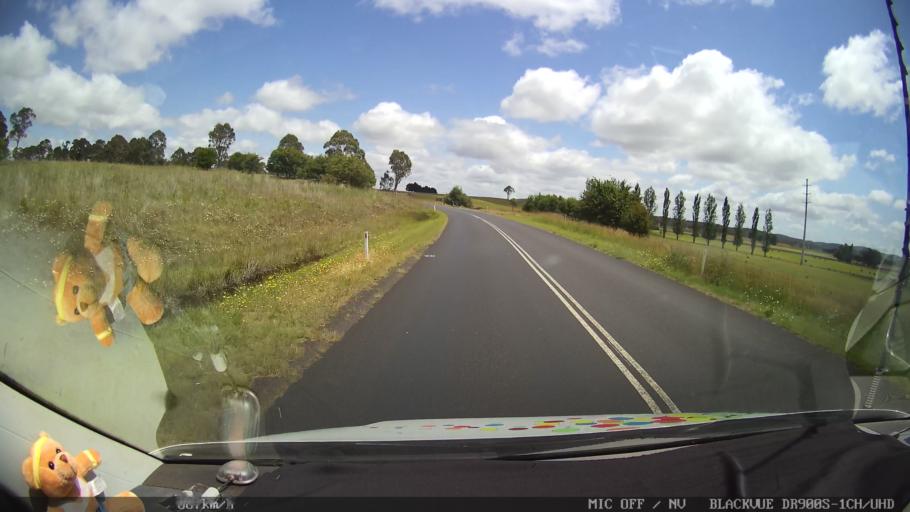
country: AU
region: New South Wales
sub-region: Glen Innes Severn
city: Glen Innes
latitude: -29.7007
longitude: 151.7187
